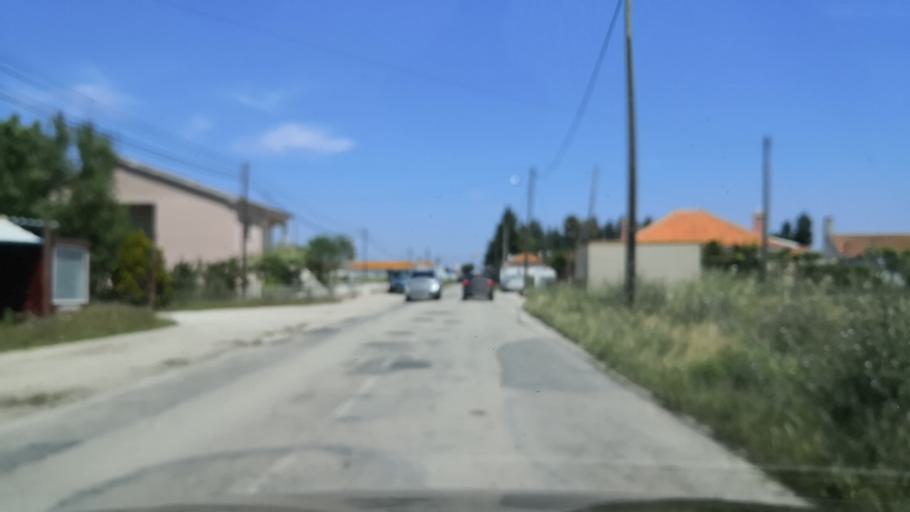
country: PT
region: Setubal
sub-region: Palmela
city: Palmela
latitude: 38.6069
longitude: -8.7783
